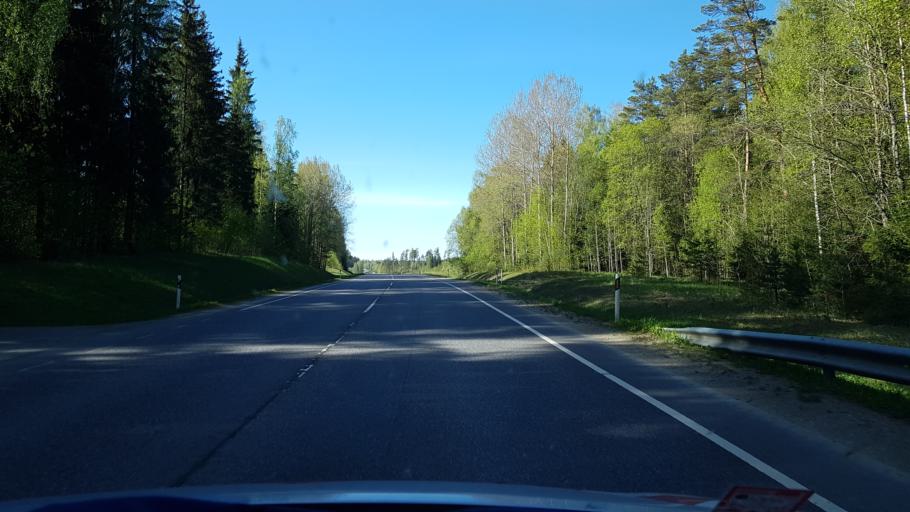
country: EE
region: Tartu
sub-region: UElenurme vald
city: Ulenurme
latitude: 58.1040
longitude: 26.7400
